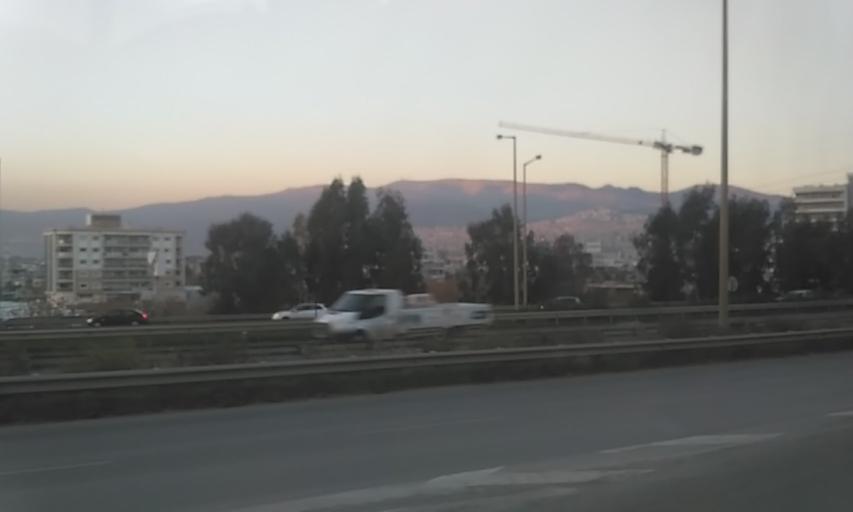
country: TR
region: Izmir
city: Bornova
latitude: 38.4356
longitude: 27.2131
